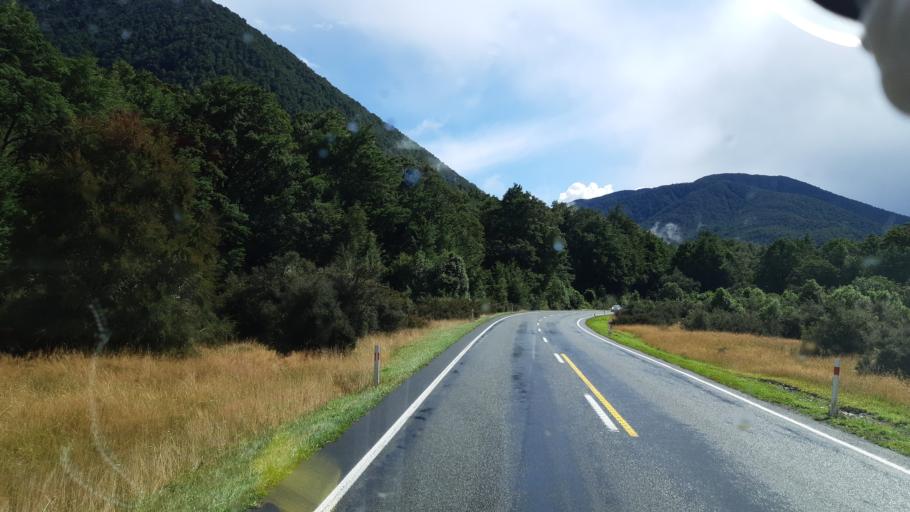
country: NZ
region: Canterbury
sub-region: Hurunui District
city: Amberley
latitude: -42.3809
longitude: 172.2853
